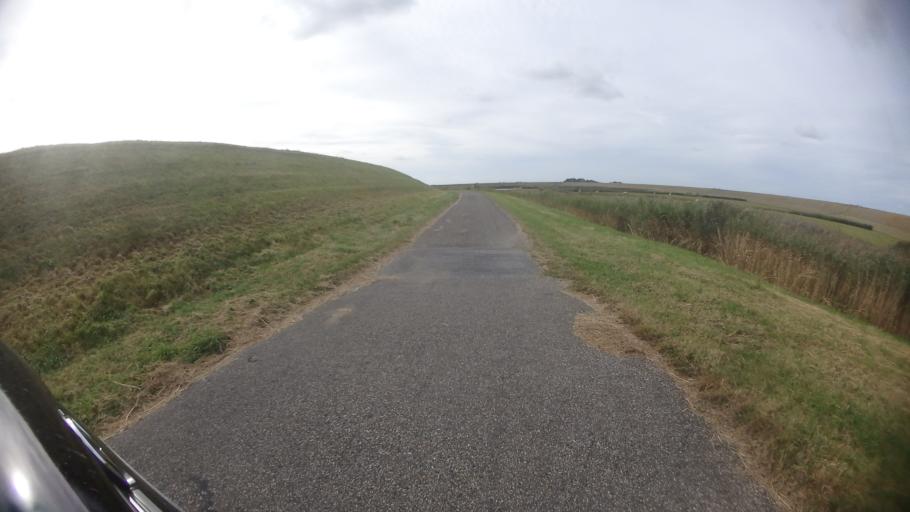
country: NL
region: North Holland
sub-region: Gemeente Texel
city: Den Burg
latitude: 53.0709
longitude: 4.8799
